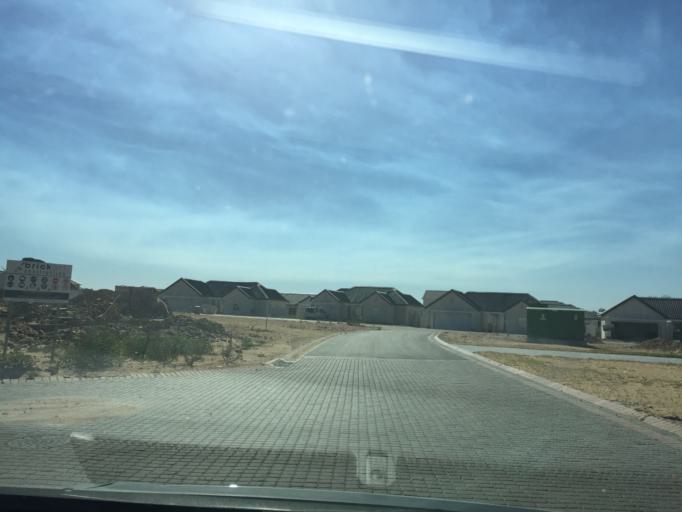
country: ZA
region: Western Cape
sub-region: Cape Winelands District Municipality
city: Paarl
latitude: -33.8063
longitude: 18.9657
